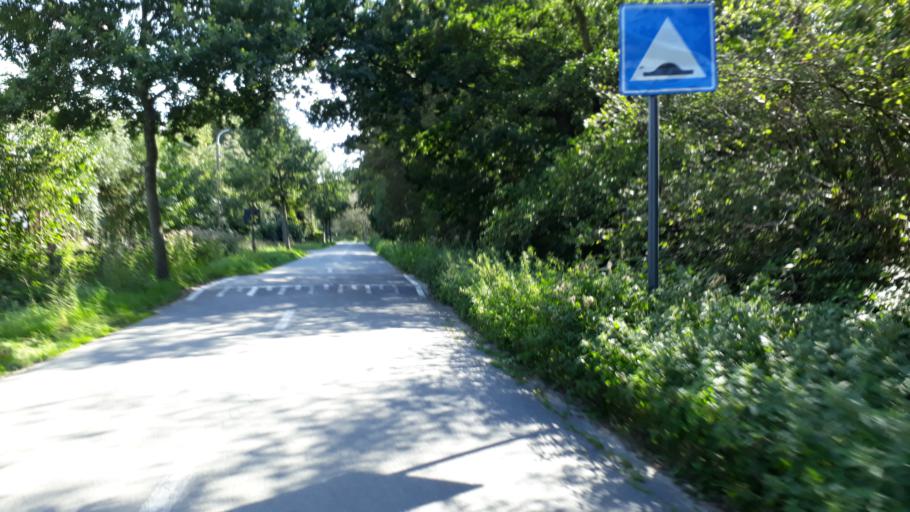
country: BE
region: Flanders
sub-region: Provincie West-Vlaanderen
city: Torhout
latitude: 51.0976
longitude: 3.0857
